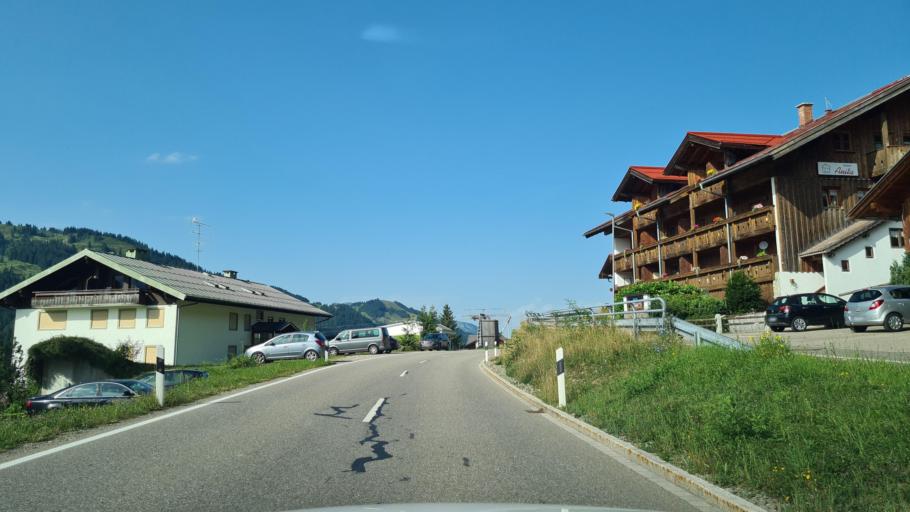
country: DE
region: Bavaria
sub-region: Swabia
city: Balderschwang
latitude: 47.4641
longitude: 10.0932
